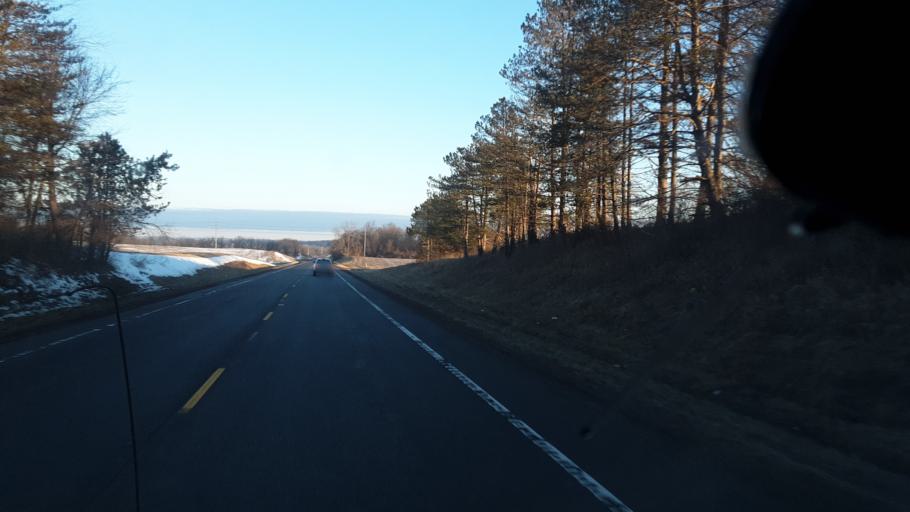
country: US
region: Ohio
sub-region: Perry County
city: Thornport
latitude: 39.8898
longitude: -82.4055
